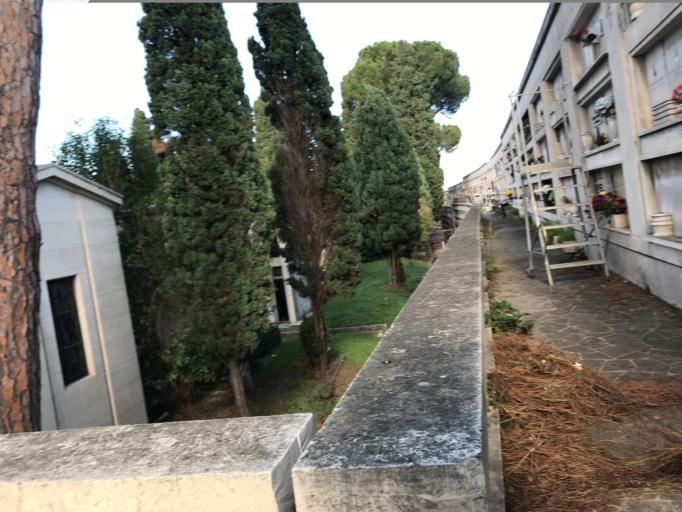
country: IT
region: Latium
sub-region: Citta metropolitana di Roma Capitale
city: Rome
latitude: 41.9056
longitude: 12.5323
